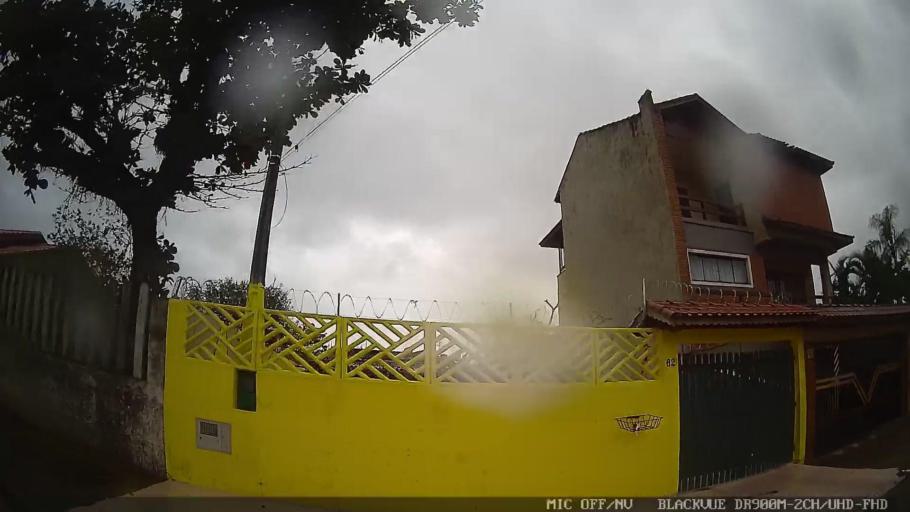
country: BR
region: Sao Paulo
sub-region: Itanhaem
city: Itanhaem
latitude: -24.1722
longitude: -46.7708
